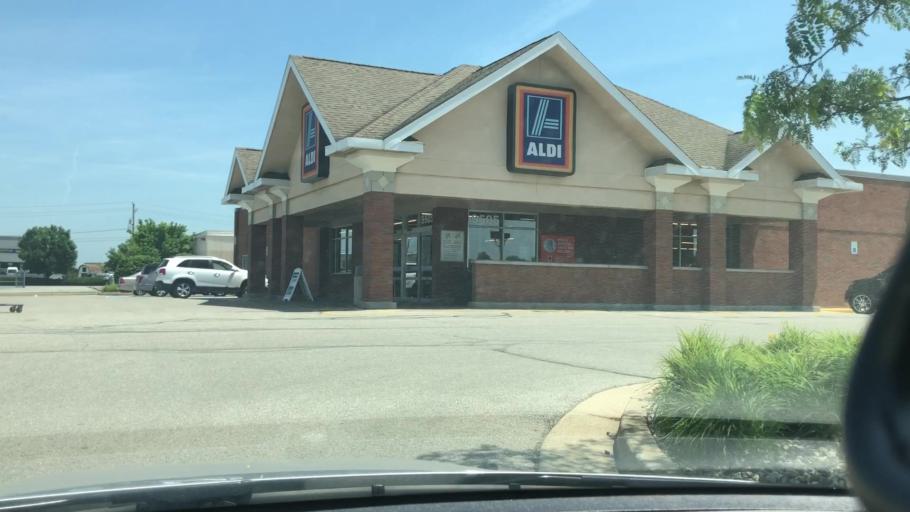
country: US
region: Indiana
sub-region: Hamilton County
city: Fishers
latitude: 39.9254
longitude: -86.0347
